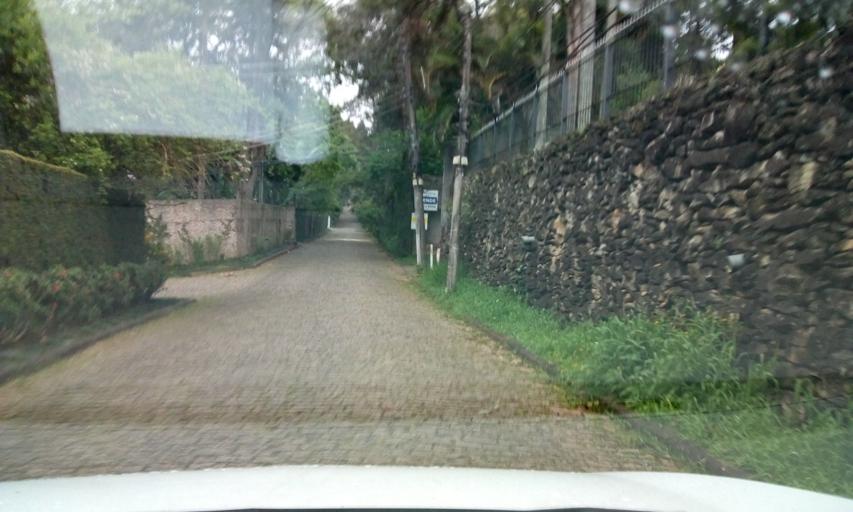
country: BR
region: Sao Paulo
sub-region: Diadema
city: Diadema
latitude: -23.6453
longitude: -46.6876
